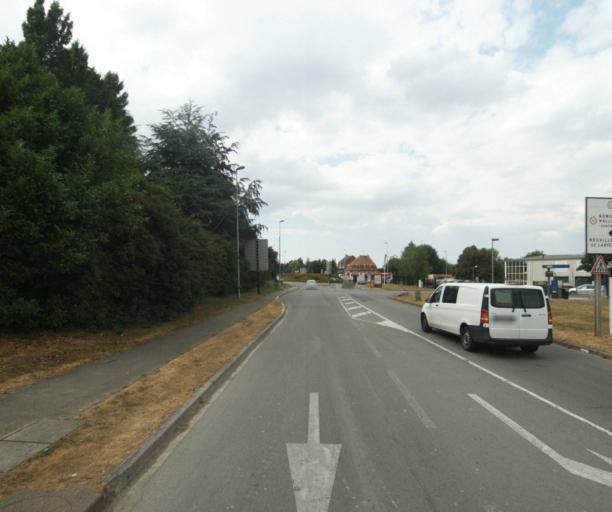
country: FR
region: Nord-Pas-de-Calais
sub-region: Departement du Nord
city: Neuville-en-Ferrain
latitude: 50.7636
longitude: 3.1567
